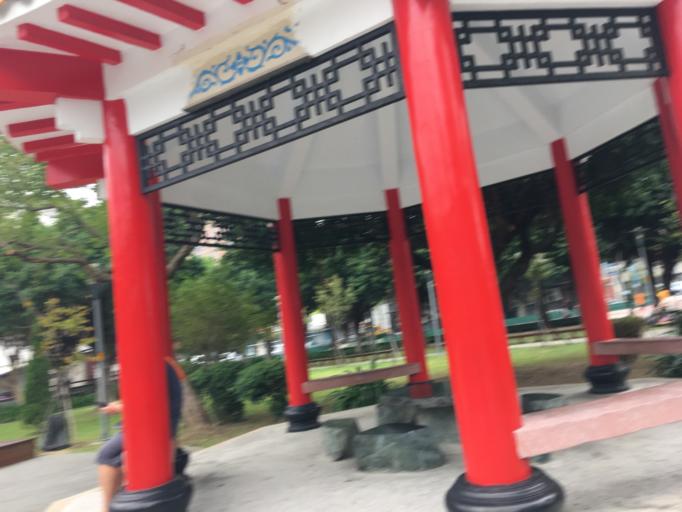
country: TW
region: Taiwan
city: Taoyuan City
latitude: 25.0202
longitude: 121.3062
